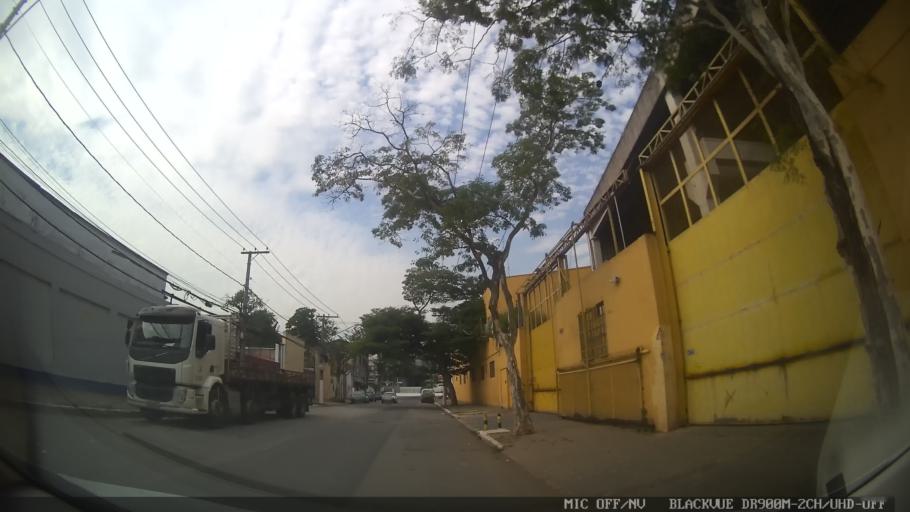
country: BR
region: Sao Paulo
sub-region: Sao Paulo
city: Sao Paulo
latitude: -23.5725
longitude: -46.6090
